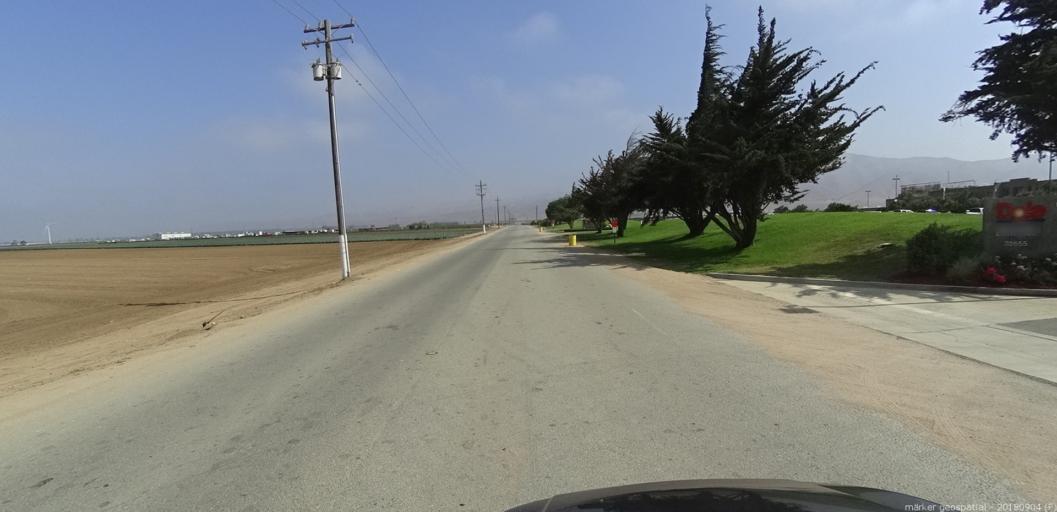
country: US
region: California
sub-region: Monterey County
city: Soledad
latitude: 36.4538
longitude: -121.3570
